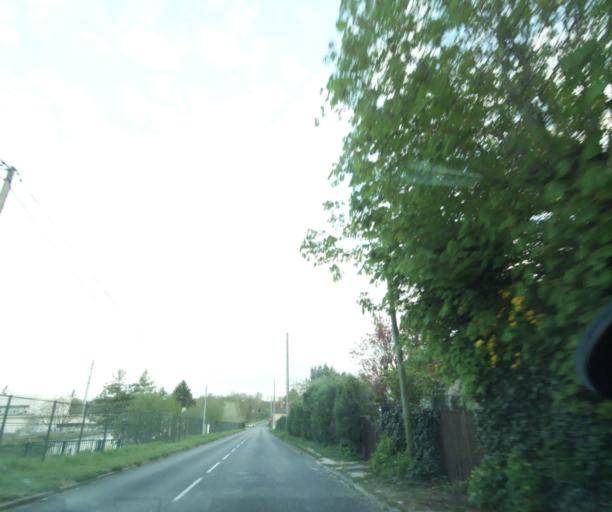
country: FR
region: Ile-de-France
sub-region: Departement de Seine-et-Marne
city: Montigny-sur-Loing
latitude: 48.3446
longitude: 2.7721
